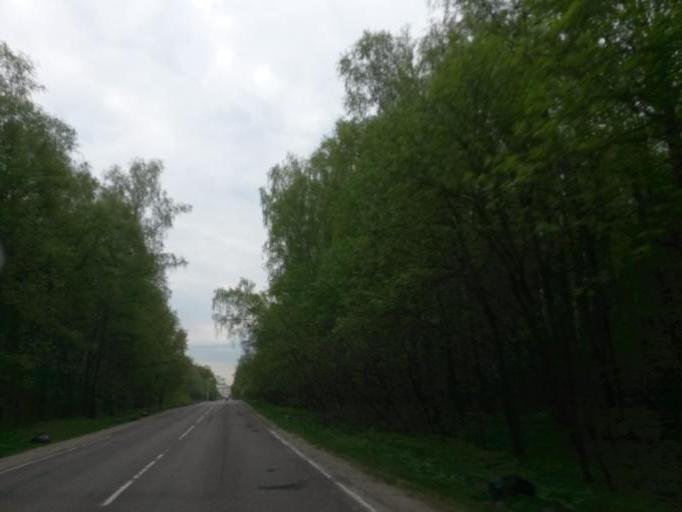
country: RU
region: Moskovskaya
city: Melikhovo
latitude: 55.1889
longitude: 37.7022
